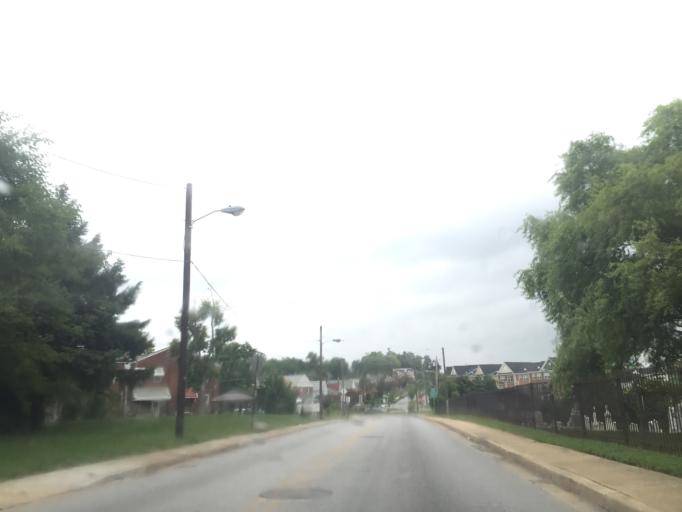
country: US
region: Maryland
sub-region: Baltimore County
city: Charlestown
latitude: 39.2876
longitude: -76.6878
